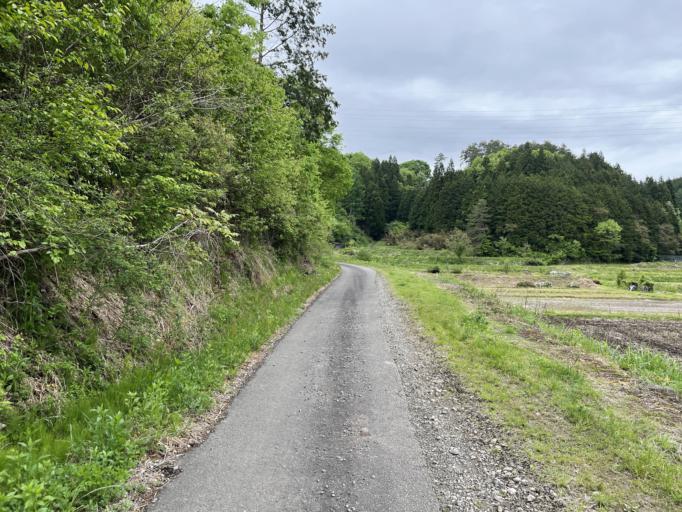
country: JP
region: Gifu
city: Takayama
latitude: 36.1590
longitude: 137.2944
